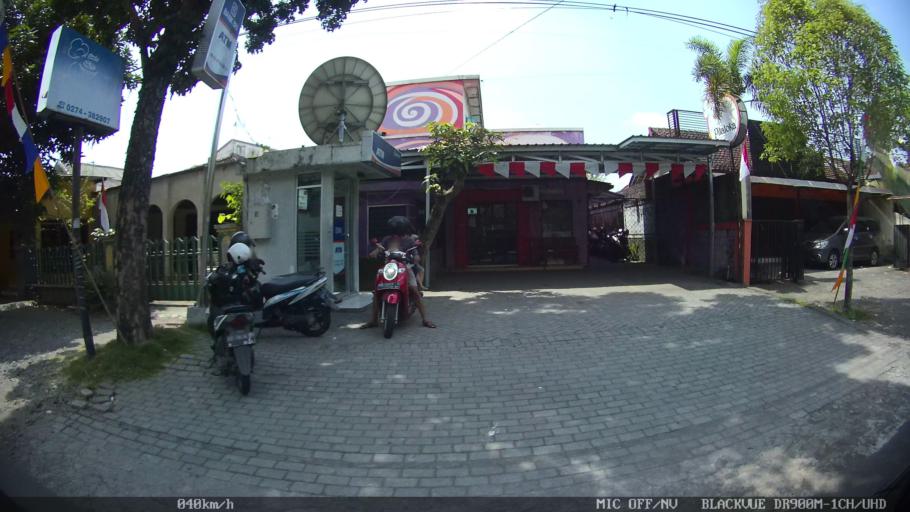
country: ID
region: Daerah Istimewa Yogyakarta
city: Yogyakarta
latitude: -7.8047
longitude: 110.3983
